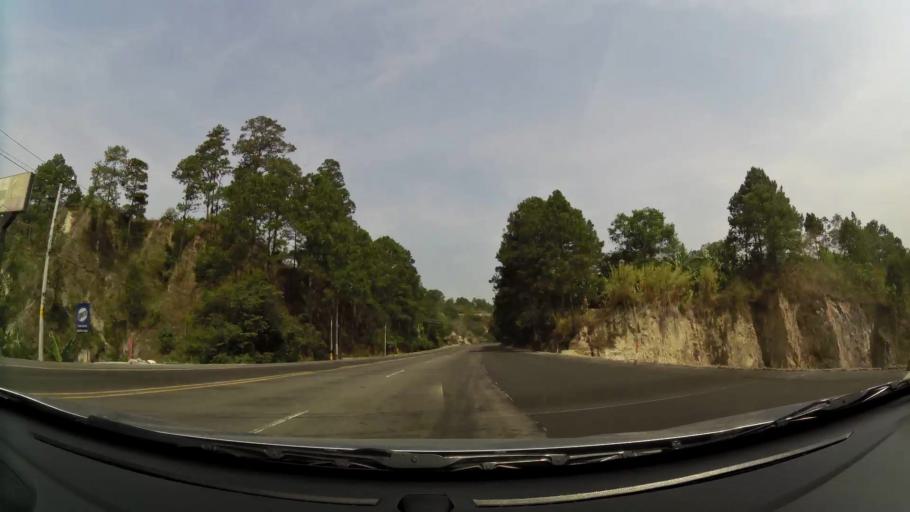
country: HN
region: Comayagua
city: Potrerillos
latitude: 14.5365
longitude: -87.8149
